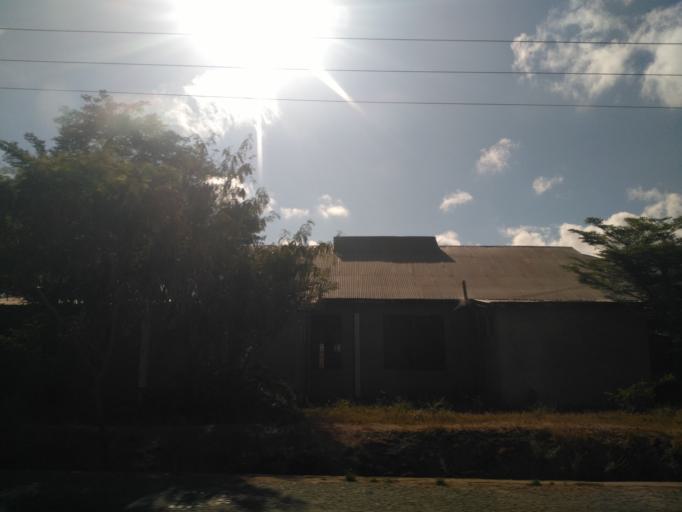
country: TZ
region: Dodoma
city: Dodoma
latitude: -6.1834
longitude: 35.7421
